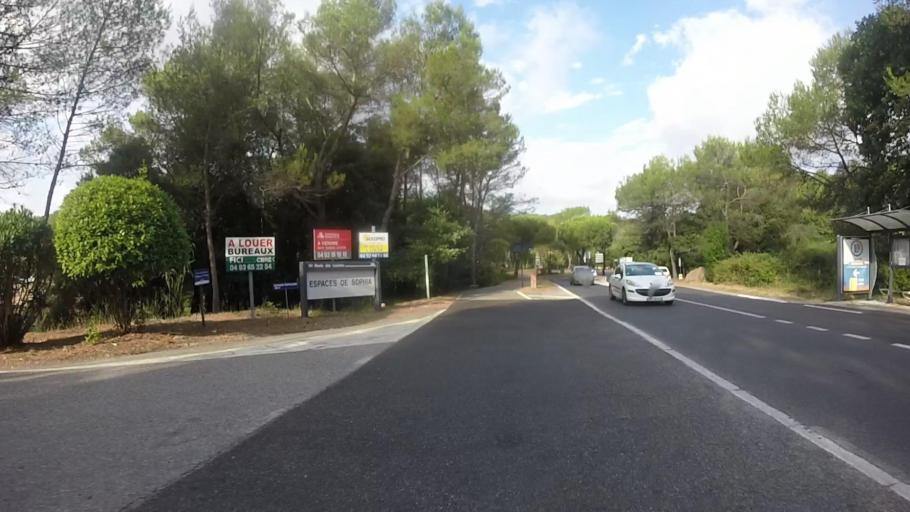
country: FR
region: Provence-Alpes-Cote d'Azur
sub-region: Departement des Alpes-Maritimes
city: Vallauris
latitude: 43.6140
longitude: 7.0469
